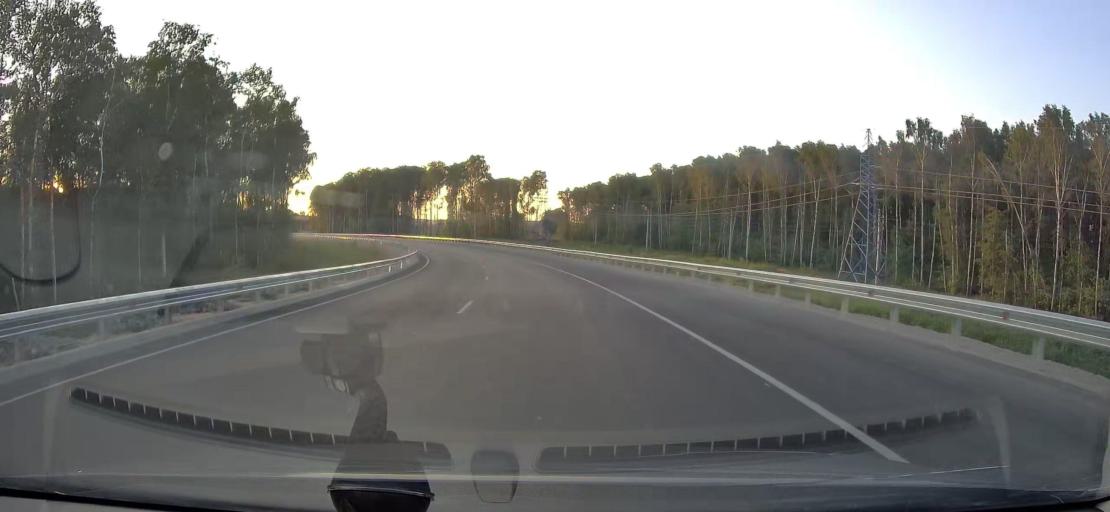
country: RU
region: Moskovskaya
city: L'vovskiy
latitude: 55.3317
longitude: 37.5366
